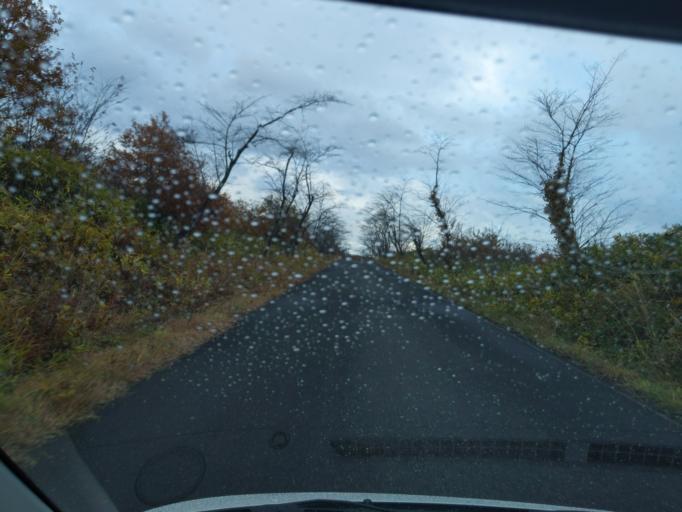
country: JP
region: Iwate
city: Mizusawa
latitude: 39.0883
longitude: 141.0084
